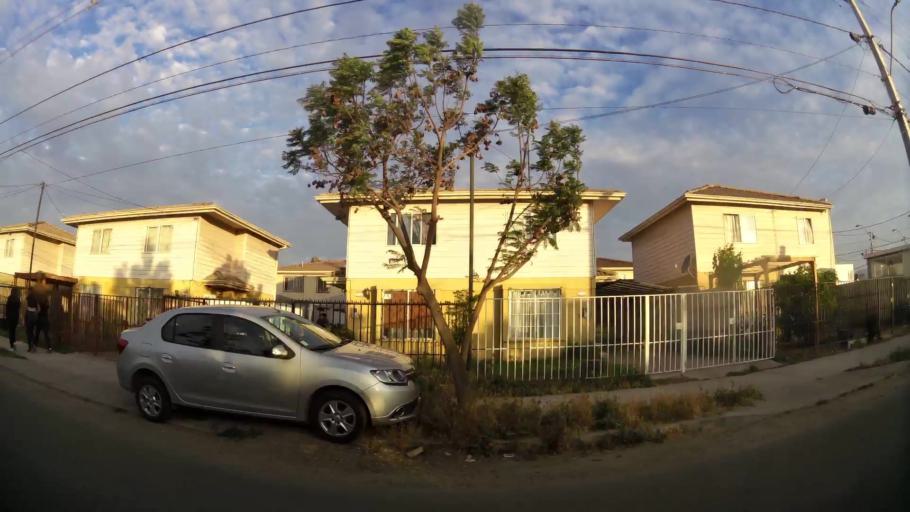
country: CL
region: Santiago Metropolitan
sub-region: Provincia de Maipo
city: San Bernardo
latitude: -33.6280
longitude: -70.6885
